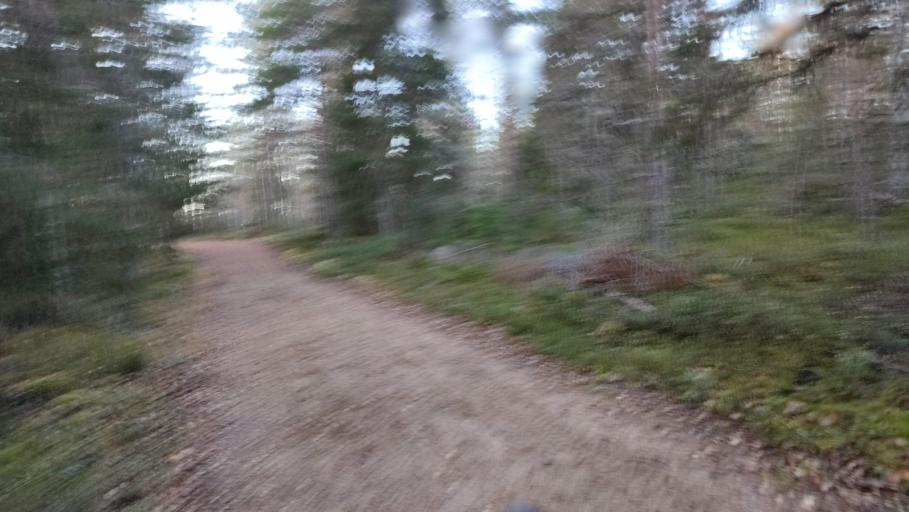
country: FI
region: Southern Ostrobothnia
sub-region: Suupohja
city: Karijoki
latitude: 62.2834
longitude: 21.6387
